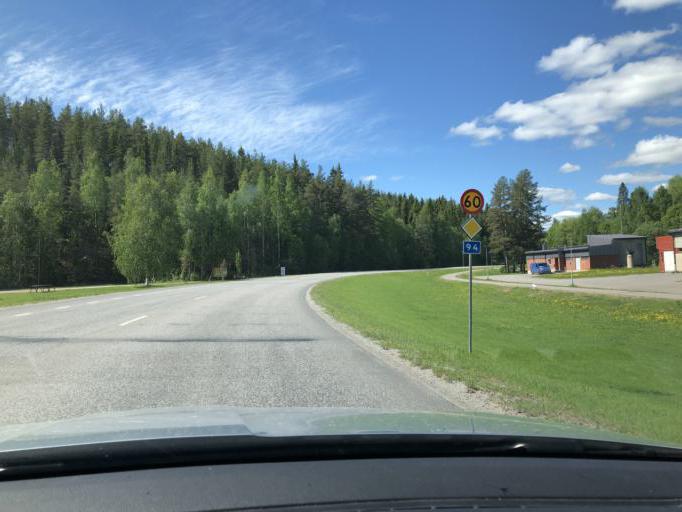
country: SE
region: Norrbotten
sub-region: Alvsbyns Kommun
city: AElvsbyn
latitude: 65.6658
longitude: 21.0322
